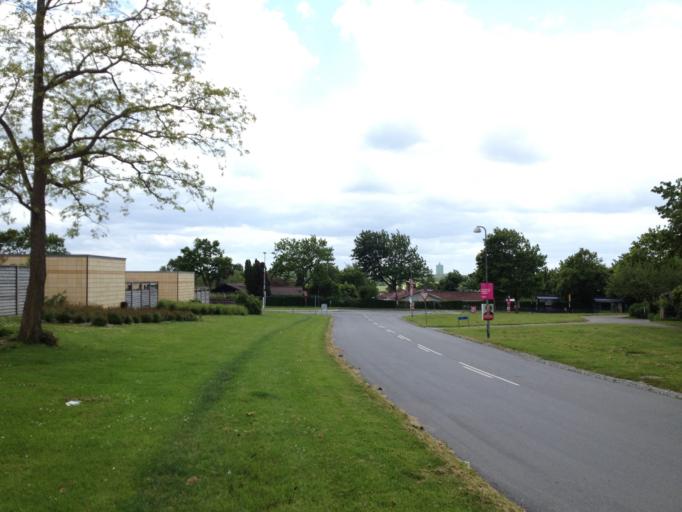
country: DK
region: Capital Region
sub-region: Fredensborg Kommune
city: Niva
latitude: 55.9371
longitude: 12.4883
